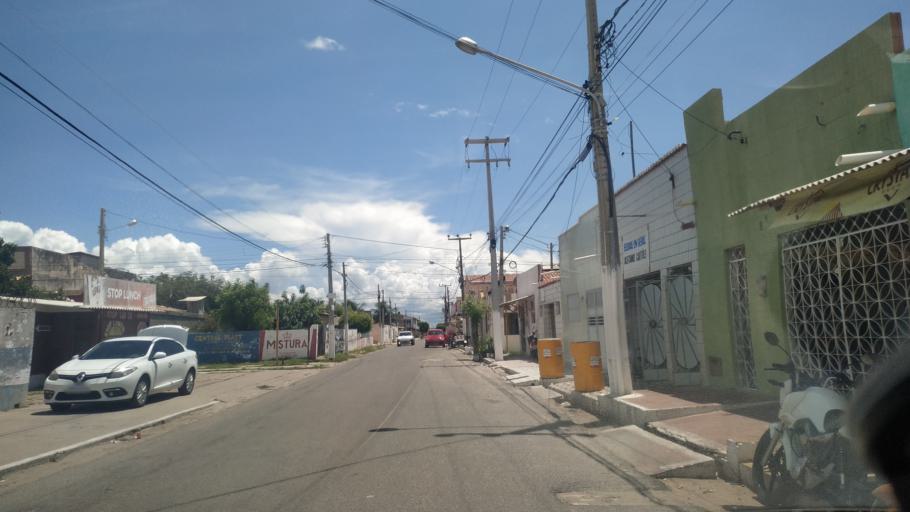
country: BR
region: Rio Grande do Norte
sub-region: Areia Branca
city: Areia Branca
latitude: -4.9538
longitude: -37.1336
